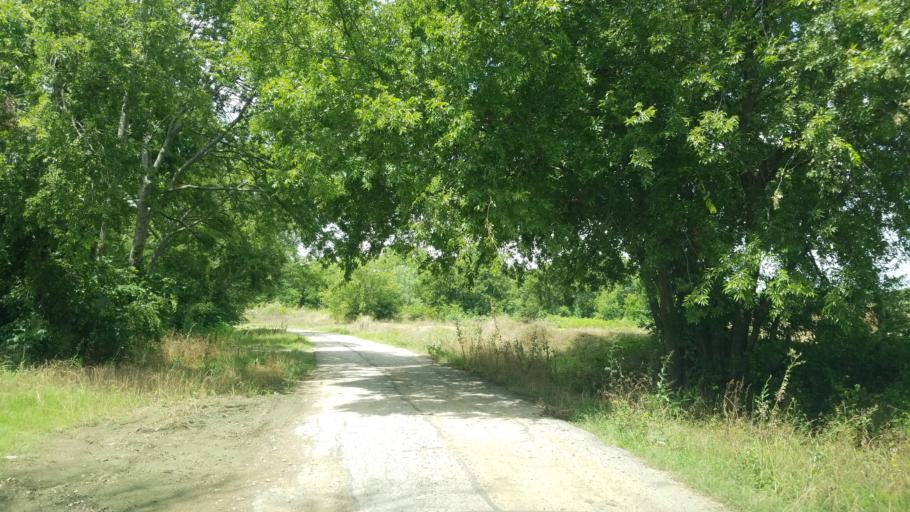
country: US
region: Texas
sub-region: Dallas County
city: Irving
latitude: 32.7819
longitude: -96.9113
